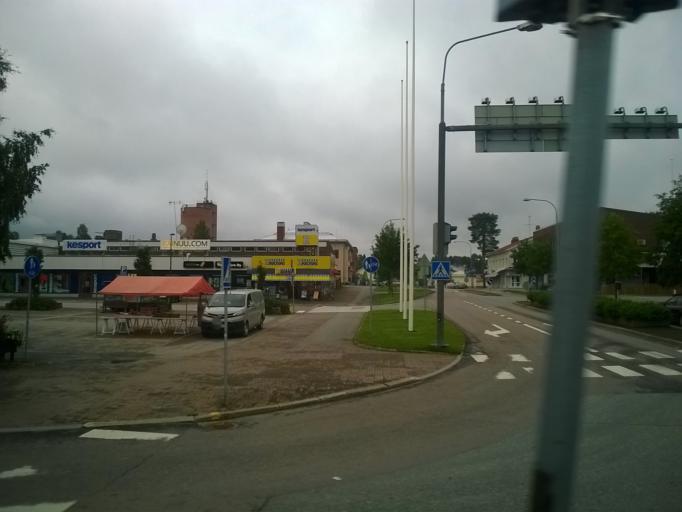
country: FI
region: Kainuu
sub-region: Kehys-Kainuu
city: Kuhmo
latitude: 64.1286
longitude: 29.5204
